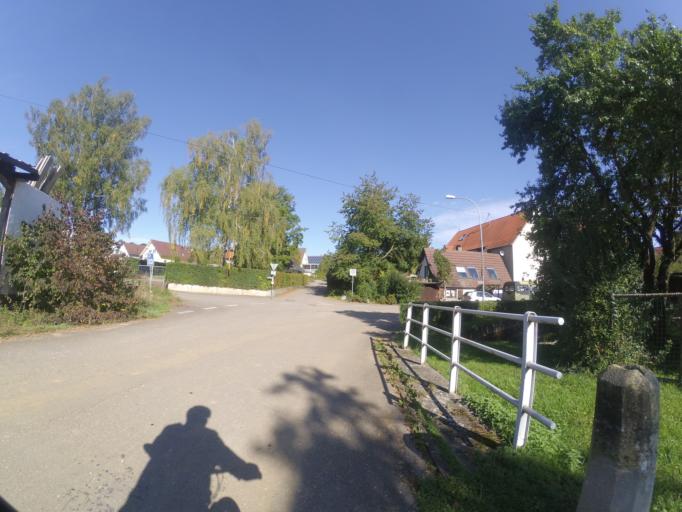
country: DE
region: Baden-Wuerttemberg
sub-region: Tuebingen Region
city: Breitingen
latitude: 48.5151
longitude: 9.9917
